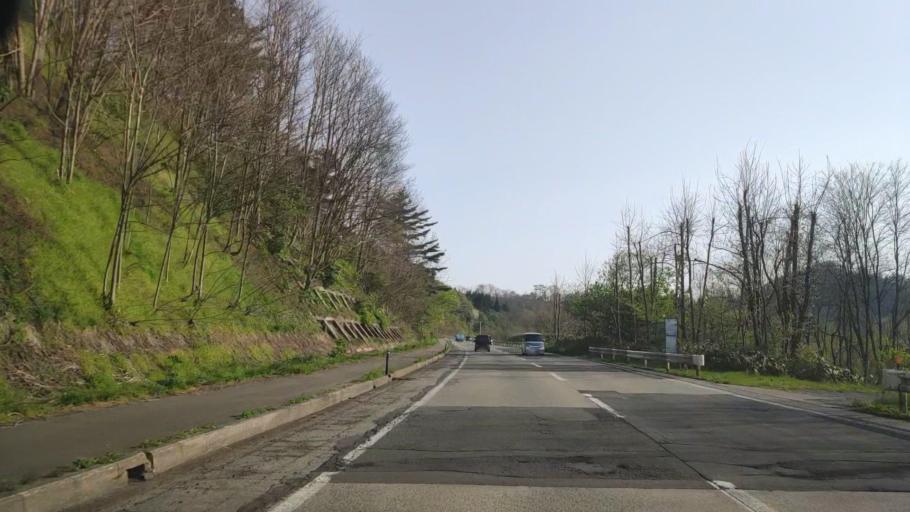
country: JP
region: Aomori
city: Aomori Shi
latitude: 40.8658
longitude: 140.8459
